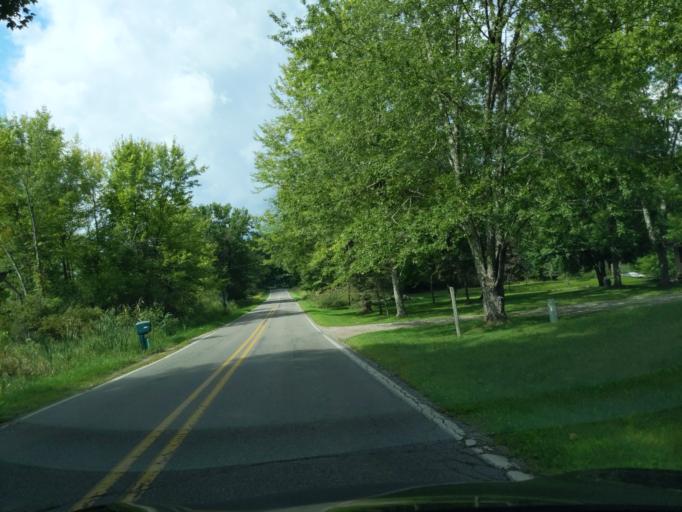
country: US
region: Michigan
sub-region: Jackson County
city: Spring Arbor
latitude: 42.3394
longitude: -84.5498
